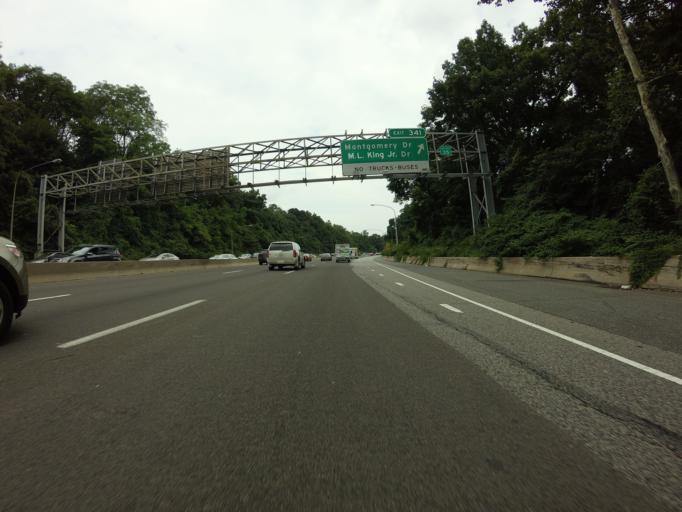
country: US
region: Pennsylvania
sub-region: Montgomery County
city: Bala-Cynwyd
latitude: 39.9825
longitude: -75.2077
